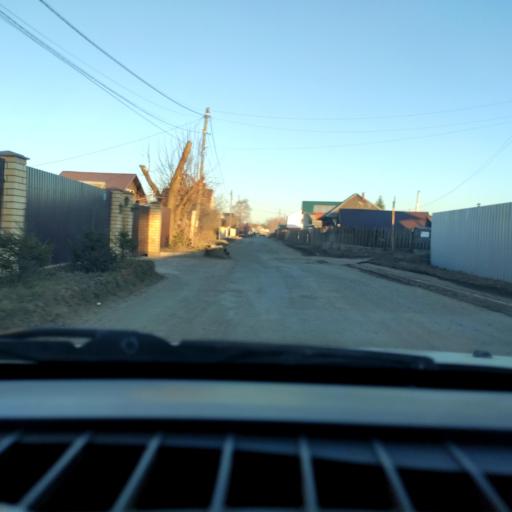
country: RU
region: Perm
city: Kultayevo
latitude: 57.9337
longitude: 56.0141
